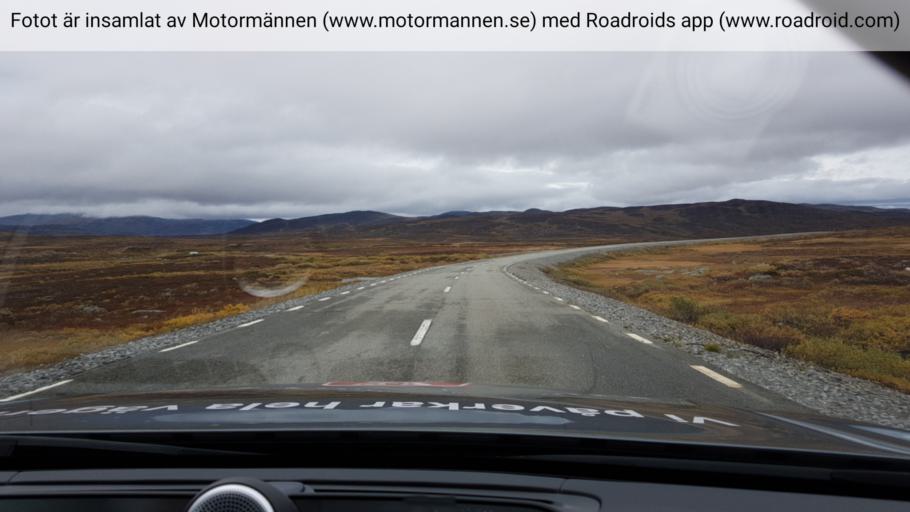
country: NO
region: Nordland
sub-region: Hattfjelldal
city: Hattfjelldal
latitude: 65.1007
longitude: 14.4682
